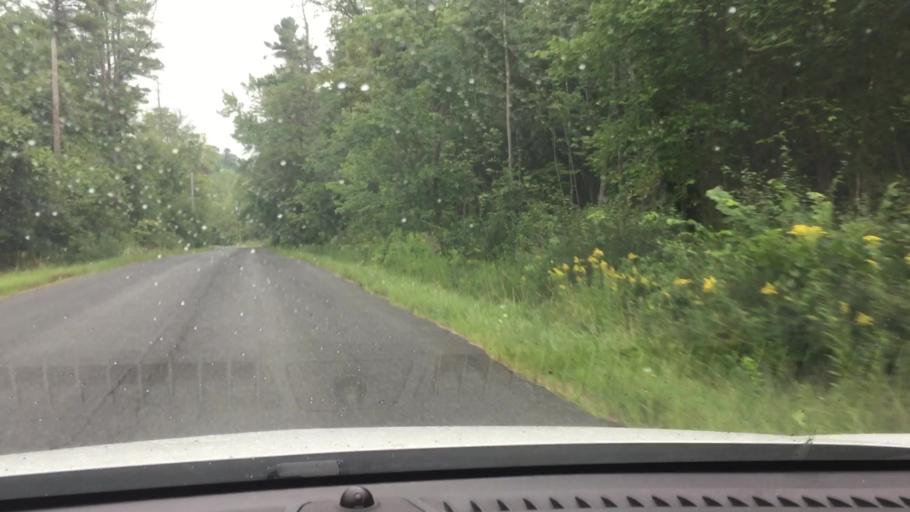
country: US
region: Massachusetts
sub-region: Berkshire County
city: Lee
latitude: 42.3074
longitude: -73.2836
